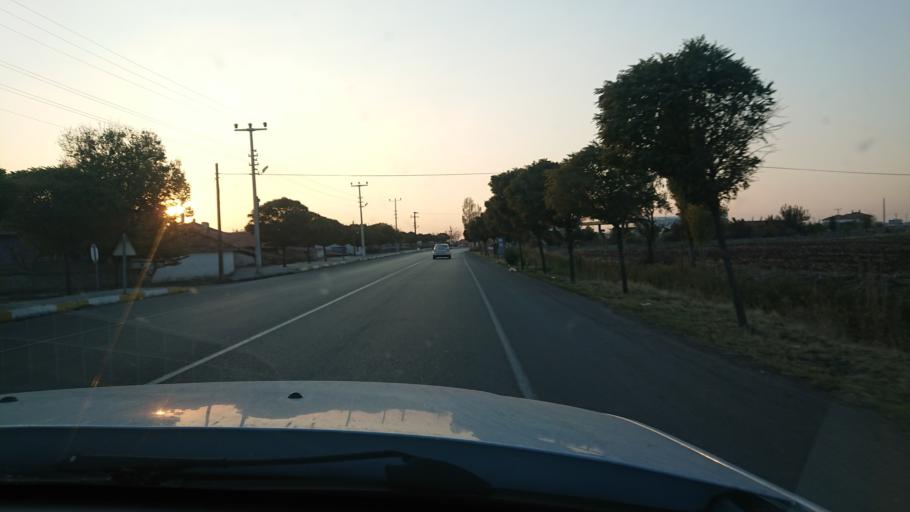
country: TR
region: Aksaray
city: Aksaray
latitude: 38.3098
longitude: 34.0651
